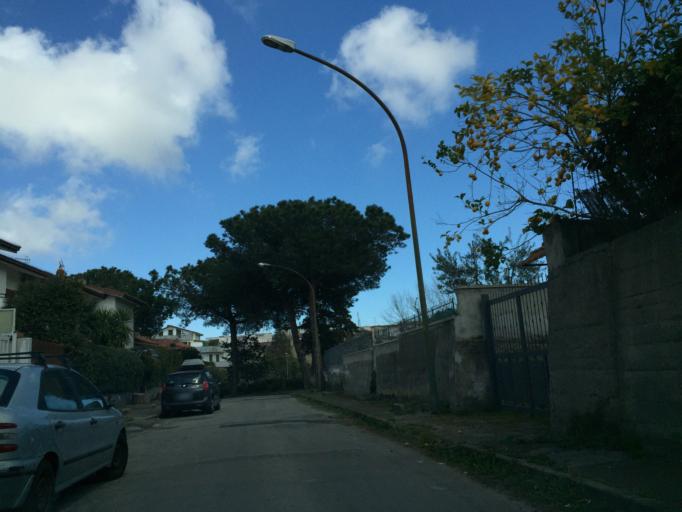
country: IT
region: Campania
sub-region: Provincia di Napoli
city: Massa di Somma
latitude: 40.8421
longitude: 14.3736
